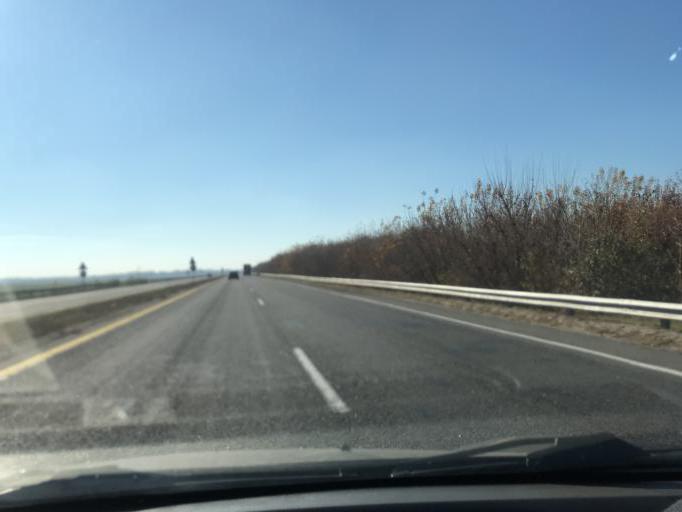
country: BY
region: Gomel
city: Horad Rechytsa
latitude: 52.3166
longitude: 30.5148
